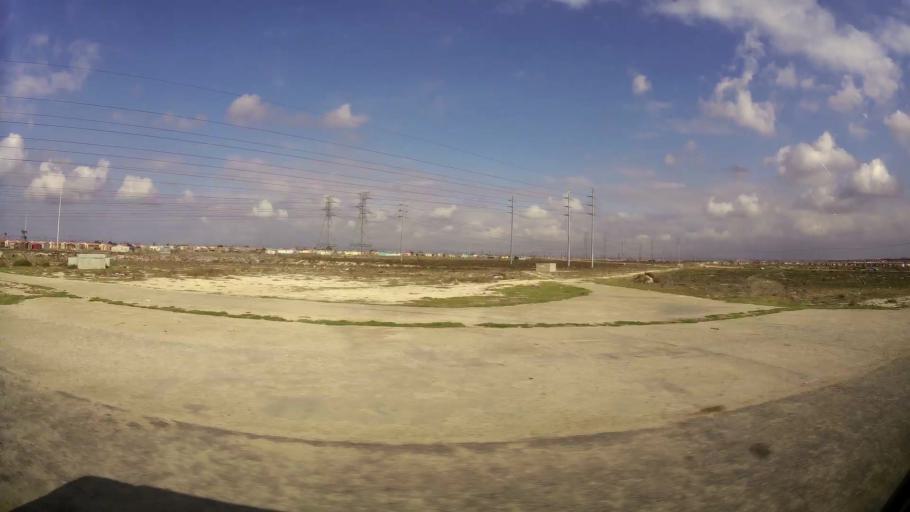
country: ZA
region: Eastern Cape
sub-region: Nelson Mandela Bay Metropolitan Municipality
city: Port Elizabeth
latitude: -33.7709
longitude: 25.5789
